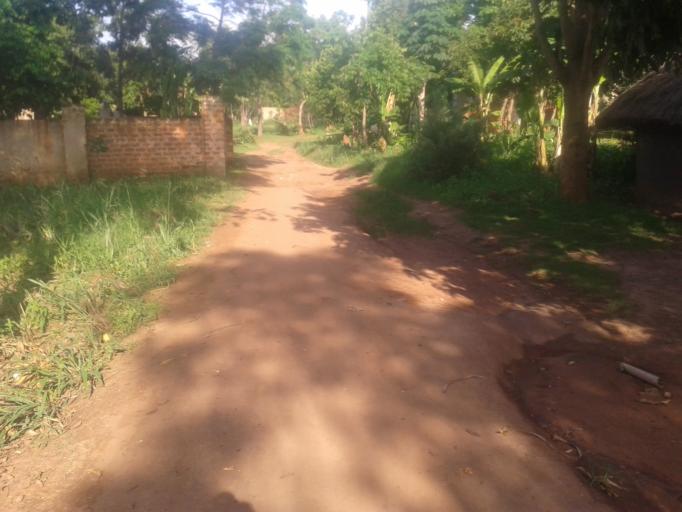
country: UG
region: Northern Region
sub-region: Gulu District
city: Gulu
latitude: 2.7900
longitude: 32.3132
